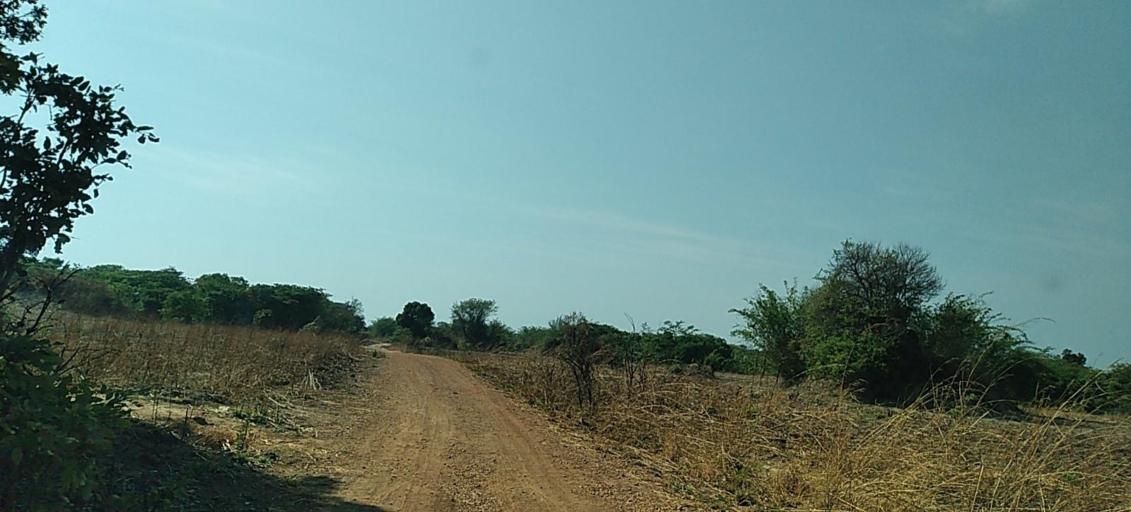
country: ZM
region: Copperbelt
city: Luanshya
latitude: -13.1942
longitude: 28.4817
